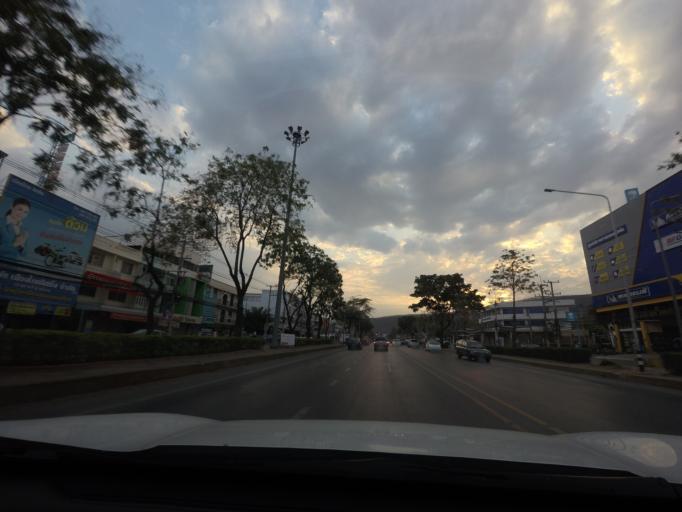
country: TH
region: Nakhon Ratchasima
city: Pak Chong
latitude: 14.7017
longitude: 101.4106
